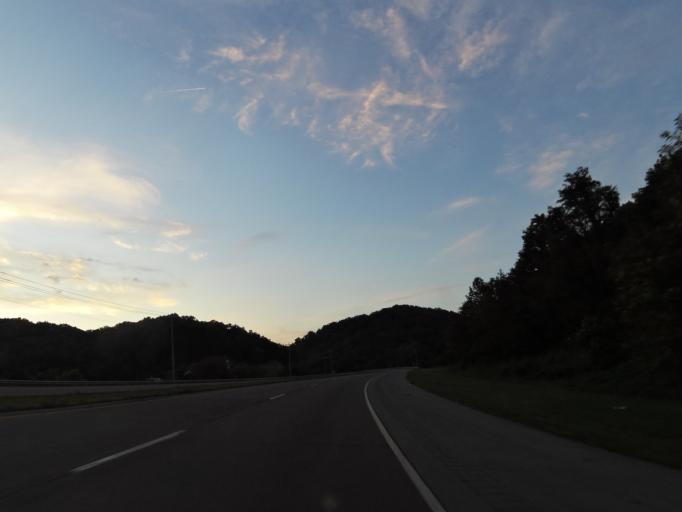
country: US
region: Tennessee
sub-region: Carter County
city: Elizabethton
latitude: 36.3639
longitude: -82.2070
